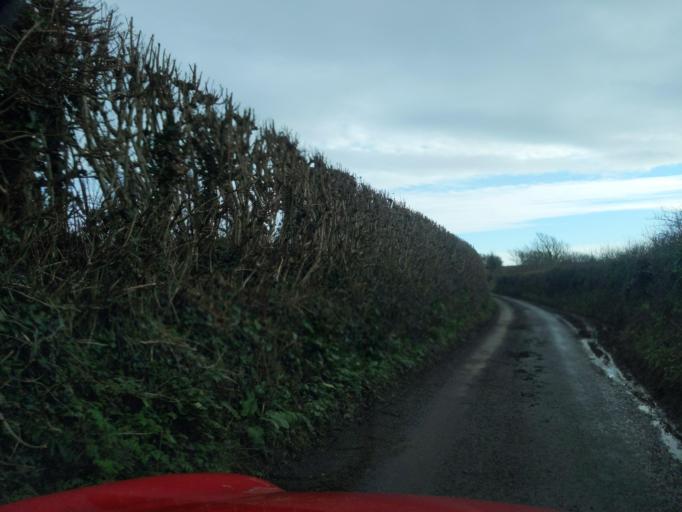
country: GB
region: England
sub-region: Devon
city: Salcombe
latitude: 50.2630
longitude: -3.6857
